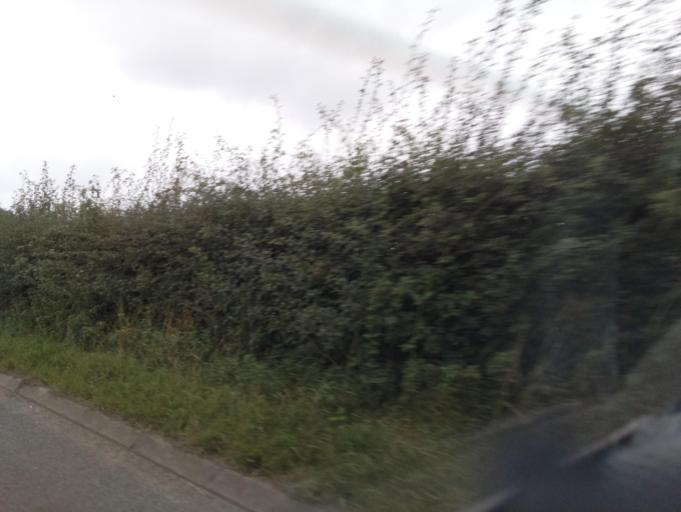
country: GB
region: England
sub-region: Staffordshire
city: Cheadle
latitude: 53.0160
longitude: -2.0131
